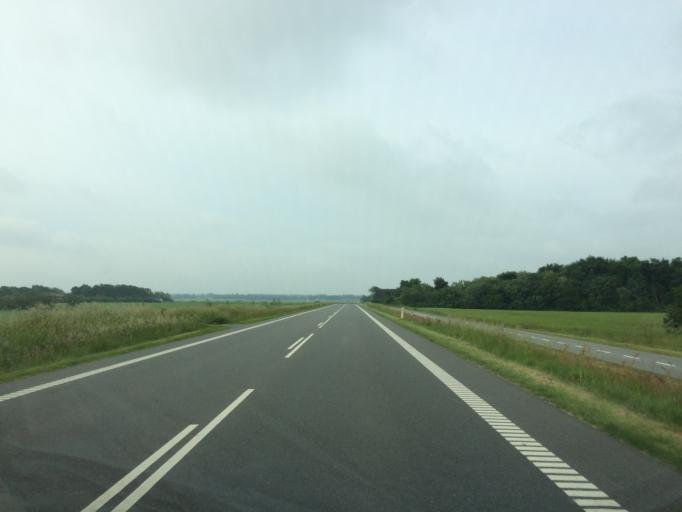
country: DK
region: Central Jutland
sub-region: Holstebro Kommune
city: Ulfborg
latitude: 56.2958
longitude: 8.3387
